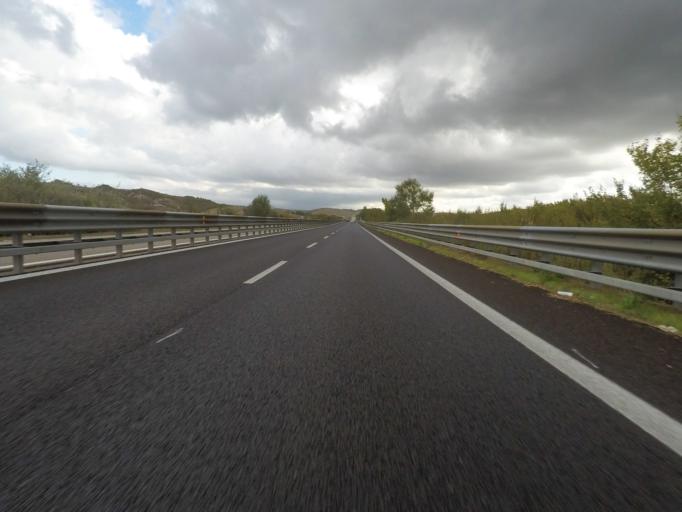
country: IT
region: Tuscany
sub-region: Provincia di Siena
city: Arbia
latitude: 43.3079
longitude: 11.4582
